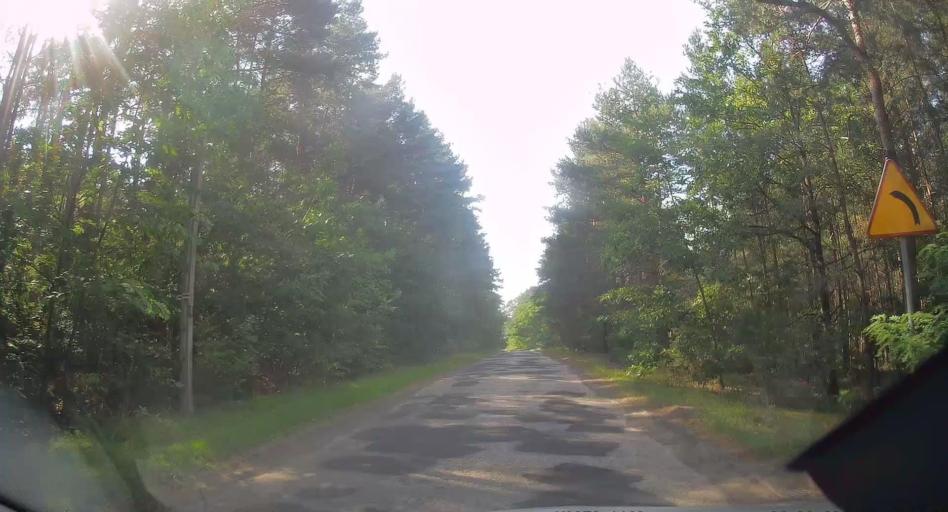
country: PL
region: Swietokrzyskie
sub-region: Powiat konecki
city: Ruda Maleniecka
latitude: 51.1279
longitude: 20.2531
